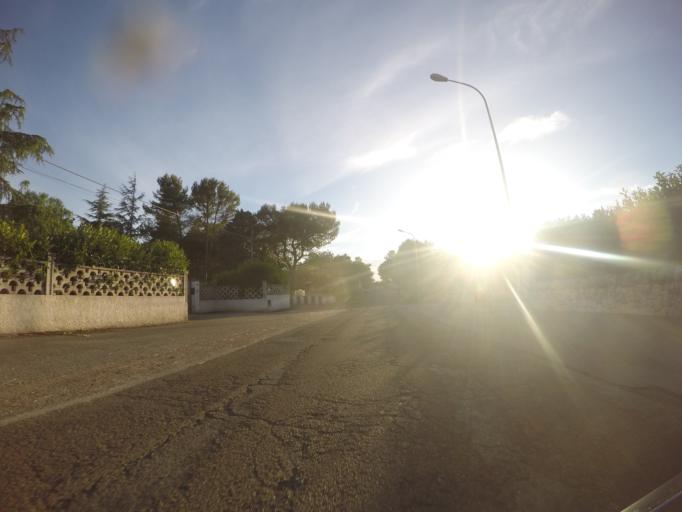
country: IT
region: Apulia
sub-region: Provincia di Taranto
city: Martina Franca
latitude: 40.6541
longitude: 17.3478
